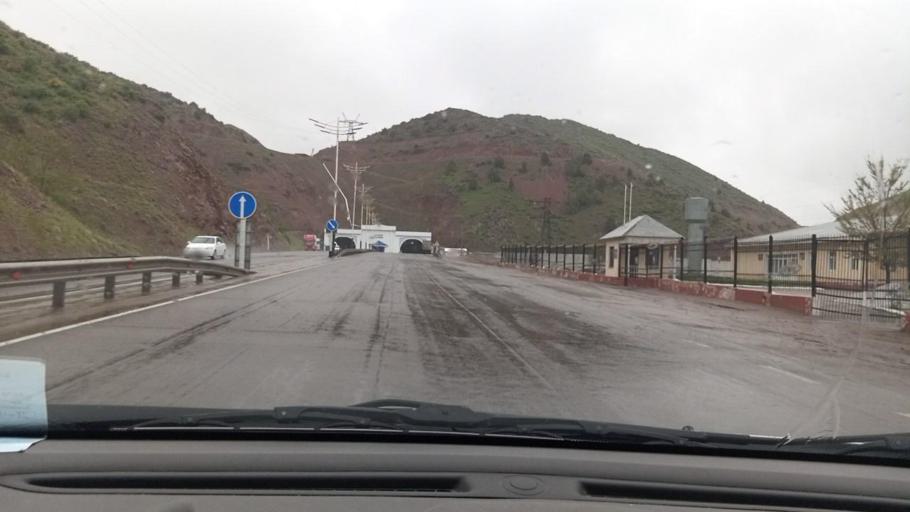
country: UZ
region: Toshkent
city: Angren
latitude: 41.0817
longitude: 70.5447
